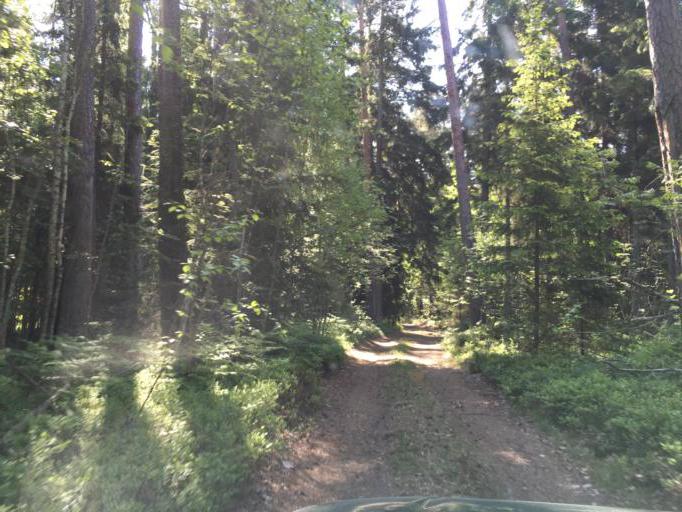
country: LV
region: Ventspils
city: Ventspils
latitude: 57.4713
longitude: 21.7700
